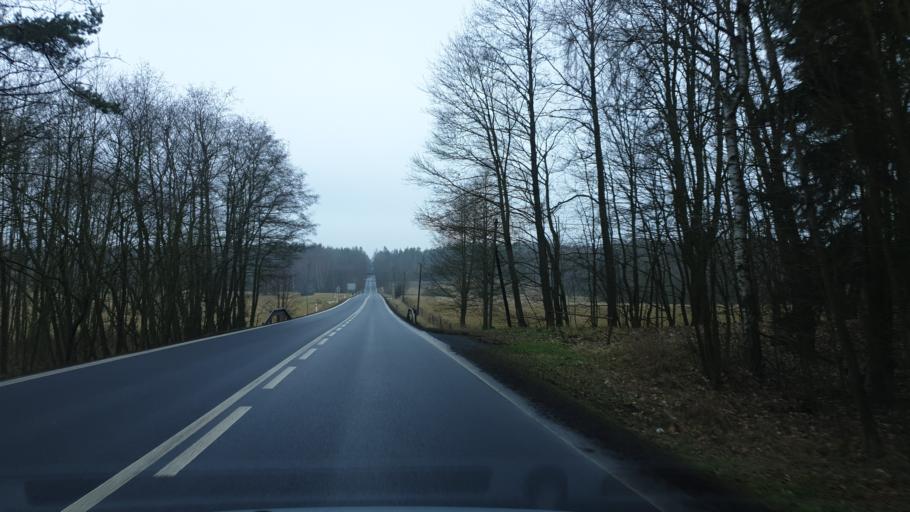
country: CZ
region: Karlovarsky
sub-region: Okres Cheb
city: Frantiskovy Lazne
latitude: 50.1409
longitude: 12.3346
